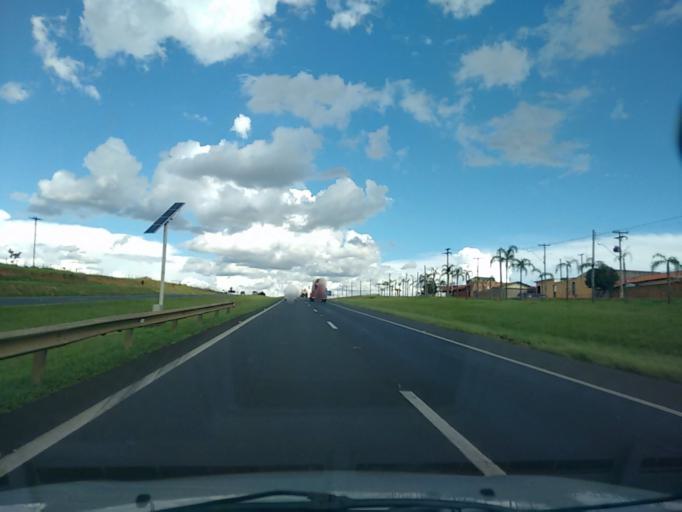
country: BR
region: Sao Paulo
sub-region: Ibate
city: Ibate
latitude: -21.9561
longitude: -47.9853
